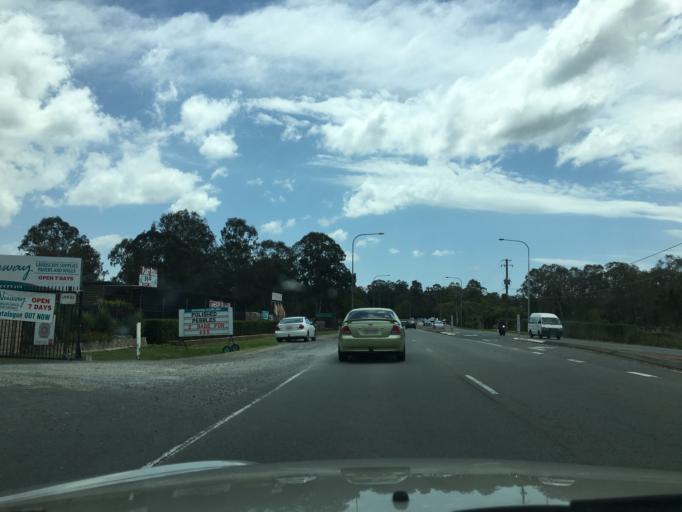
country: AU
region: Queensland
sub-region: Logan
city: Slacks Creek
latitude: -27.6503
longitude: 153.1445
